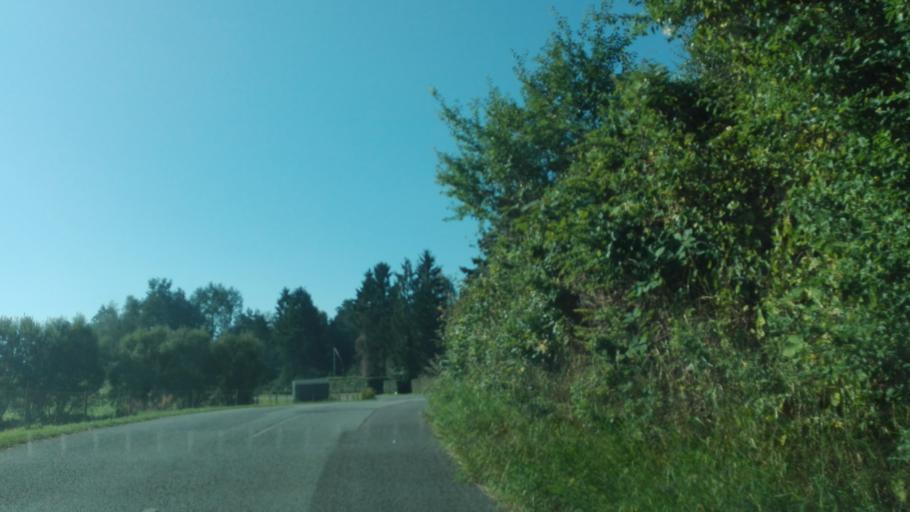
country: DK
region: Central Jutland
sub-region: Syddjurs Kommune
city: Ebeltoft
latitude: 56.2503
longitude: 10.6246
